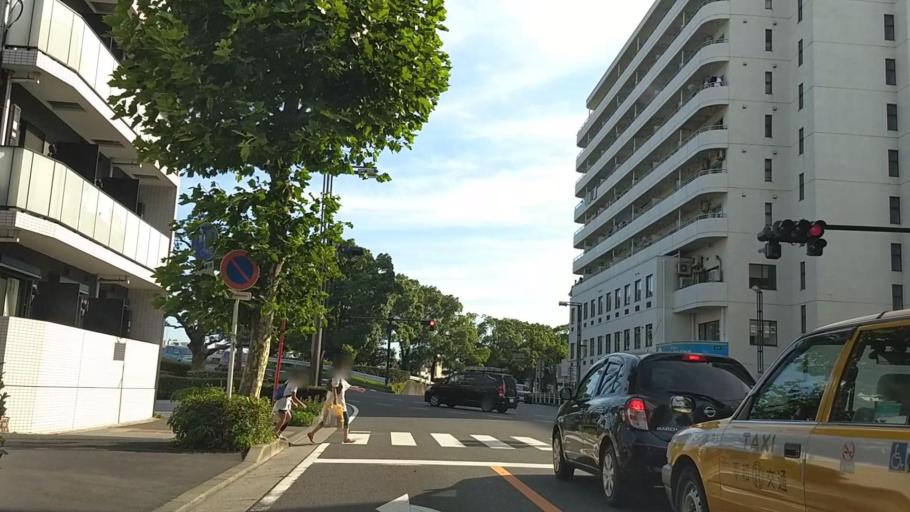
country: JP
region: Kanagawa
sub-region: Kawasaki-shi
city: Kawasaki
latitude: 35.5074
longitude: 139.6839
